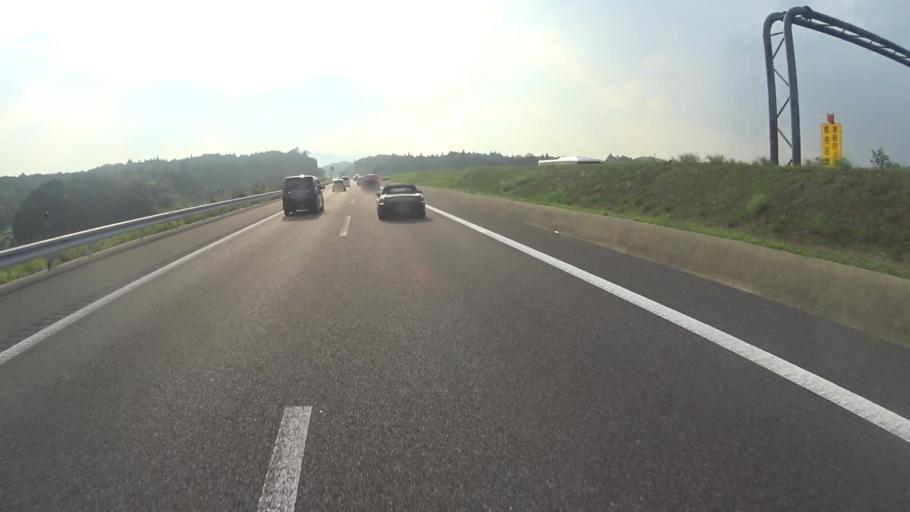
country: JP
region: Shiga Prefecture
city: Hino
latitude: 34.9254
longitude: 136.2563
